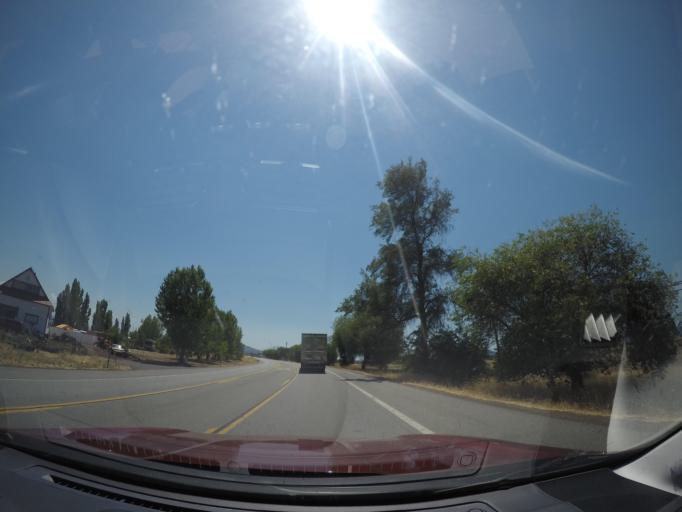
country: US
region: California
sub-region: Shasta County
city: Burney
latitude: 41.0487
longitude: -121.4058
